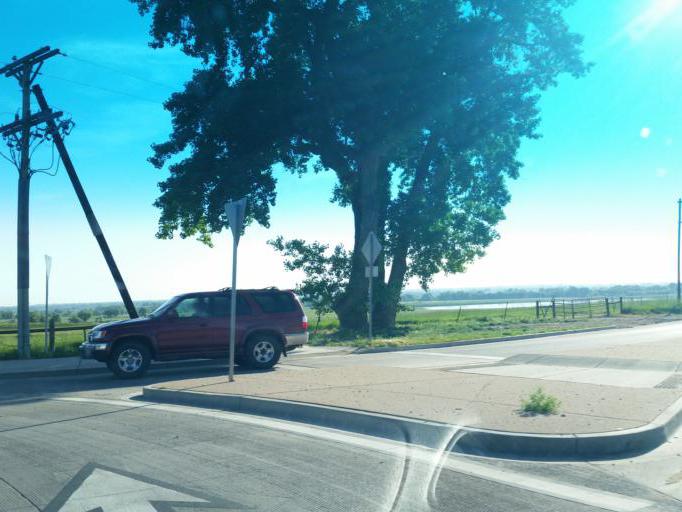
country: US
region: Colorado
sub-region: Larimer County
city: Fort Collins
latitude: 40.5377
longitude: -105.0200
